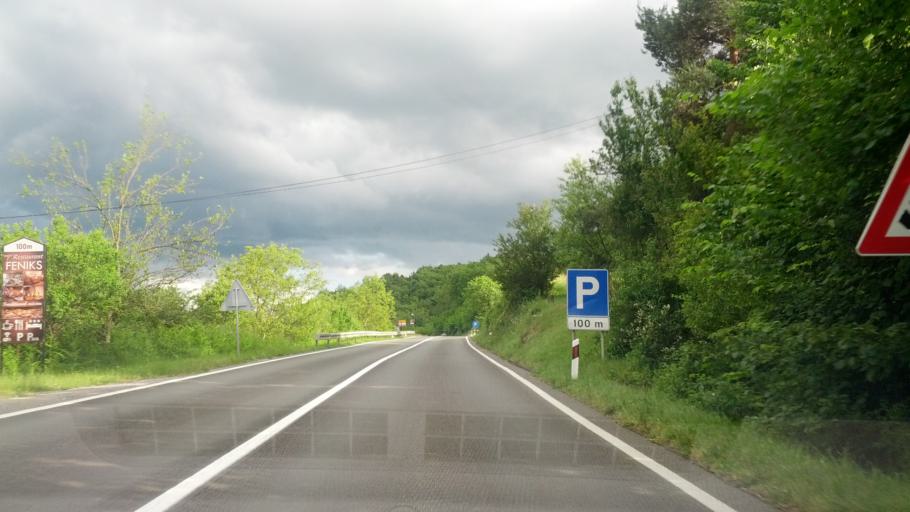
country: HR
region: Karlovacka
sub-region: Grad Karlovac
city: Slunj
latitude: 45.1029
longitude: 15.5883
